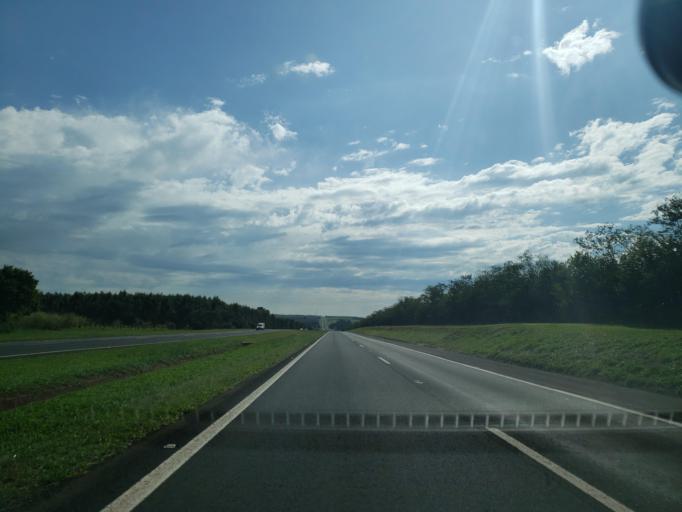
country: BR
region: Sao Paulo
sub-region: Pirajui
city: Pirajui
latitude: -21.9057
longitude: -49.5235
